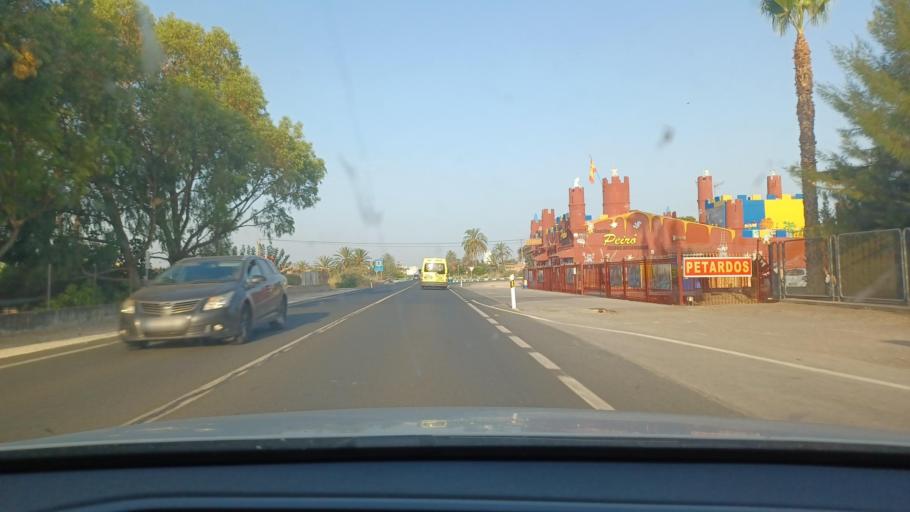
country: ES
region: Valencia
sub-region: Provincia de Alicante
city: Elche
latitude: 38.2775
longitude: -0.6511
